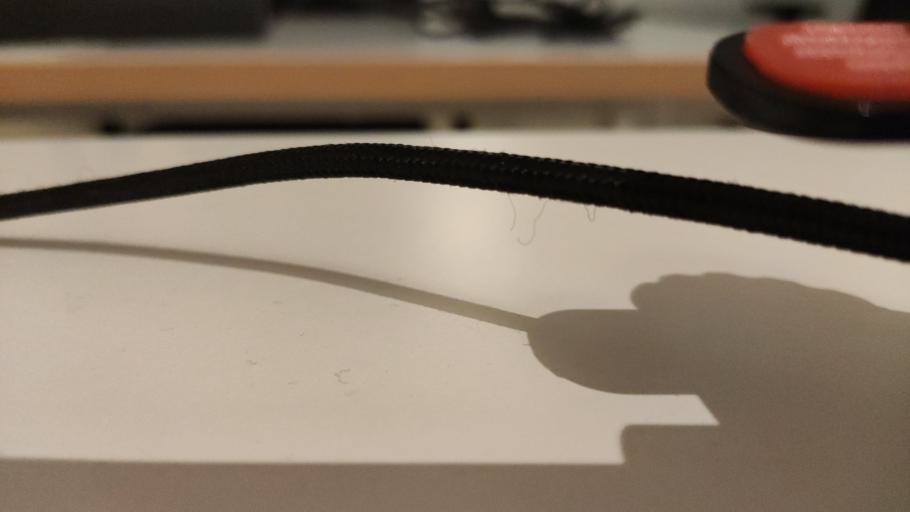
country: RU
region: Moskovskaya
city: Kurovskoye
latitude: 55.5415
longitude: 38.8731
